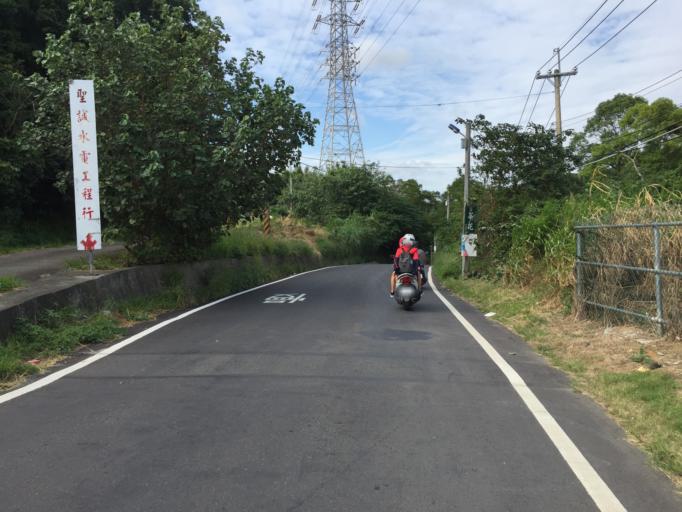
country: TW
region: Taiwan
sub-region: Hsinchu
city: Hsinchu
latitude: 24.7598
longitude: 120.9430
